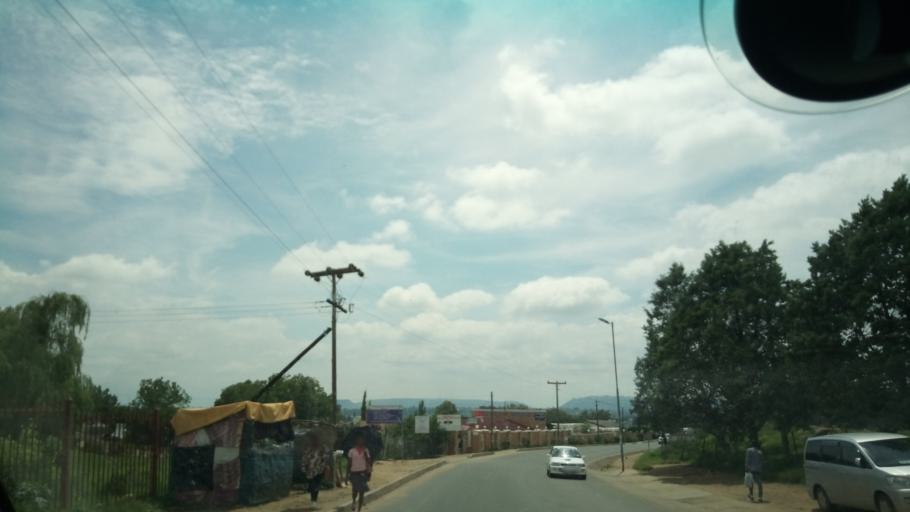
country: LS
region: Maseru
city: Maseru
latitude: -29.3230
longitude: 27.5009
